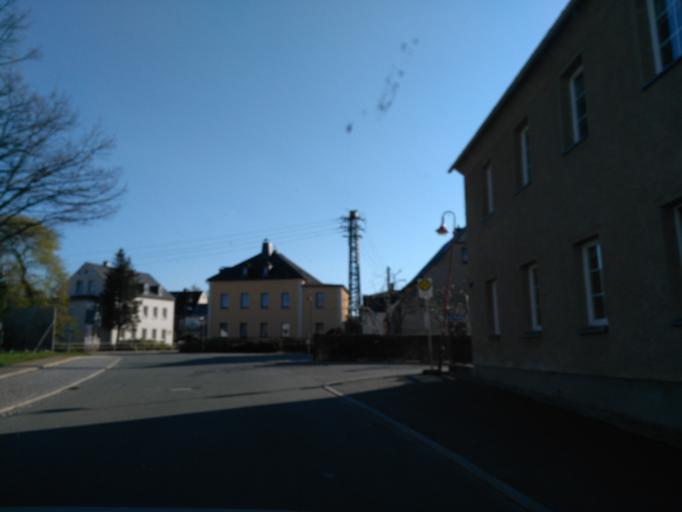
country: DE
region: Saxony
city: Crottendorf
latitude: 50.5116
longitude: 12.9380
